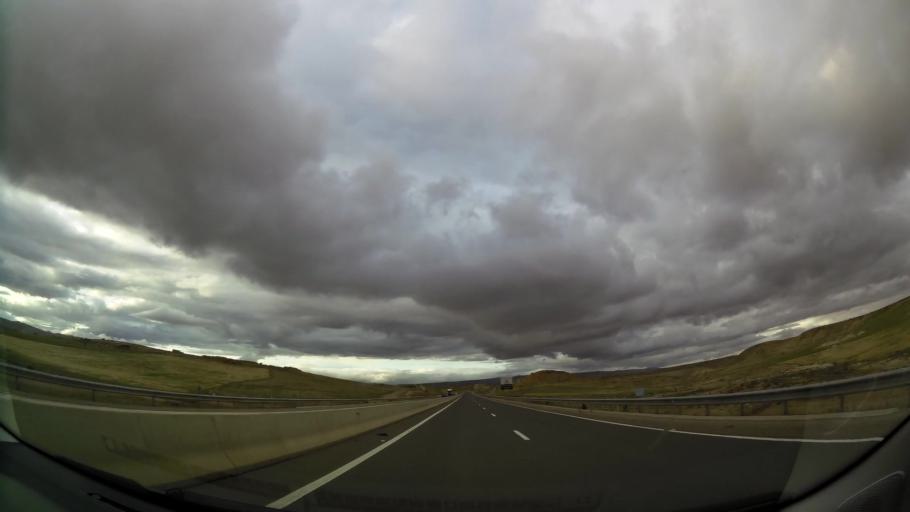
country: MA
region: Taza-Al Hoceima-Taounate
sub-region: Taza
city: Taza
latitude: 34.2922
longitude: -3.7807
